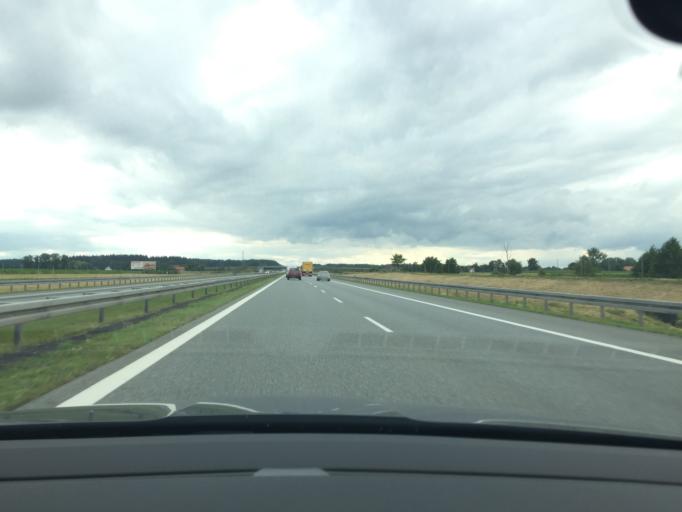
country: PL
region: Greater Poland Voivodeship
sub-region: Powiat nowotomyski
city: Kuslin
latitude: 52.3796
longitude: 16.3126
